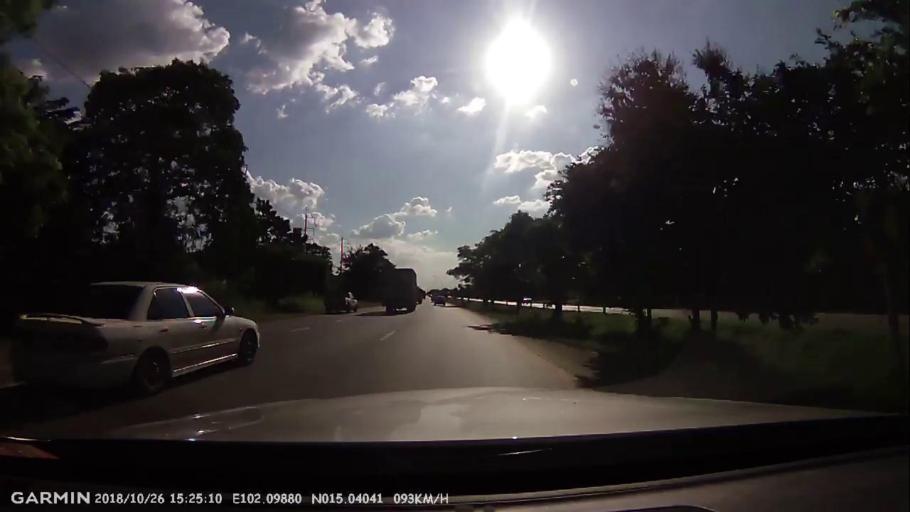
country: TH
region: Nakhon Ratchasima
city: Nakhon Ratchasima
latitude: 15.0404
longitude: 102.0987
